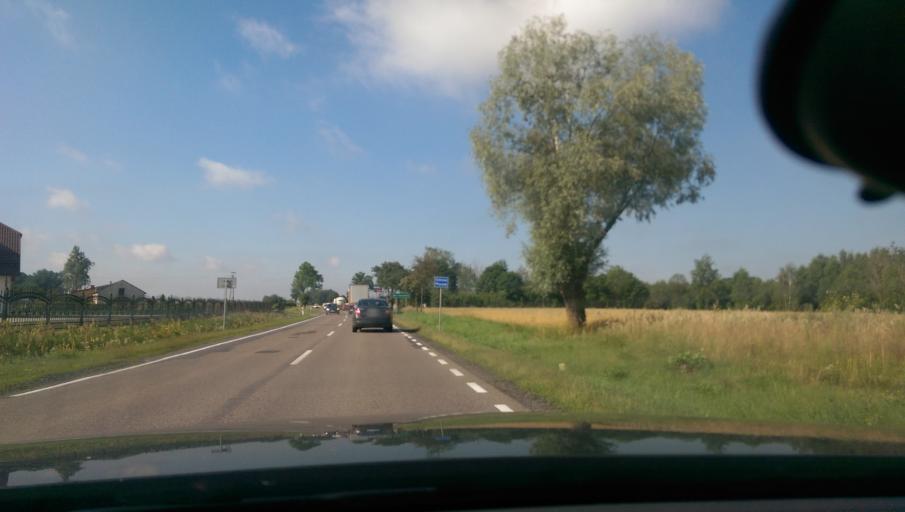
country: PL
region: Masovian Voivodeship
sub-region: Powiat plonski
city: Sochocin
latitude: 52.6544
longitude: 20.4314
